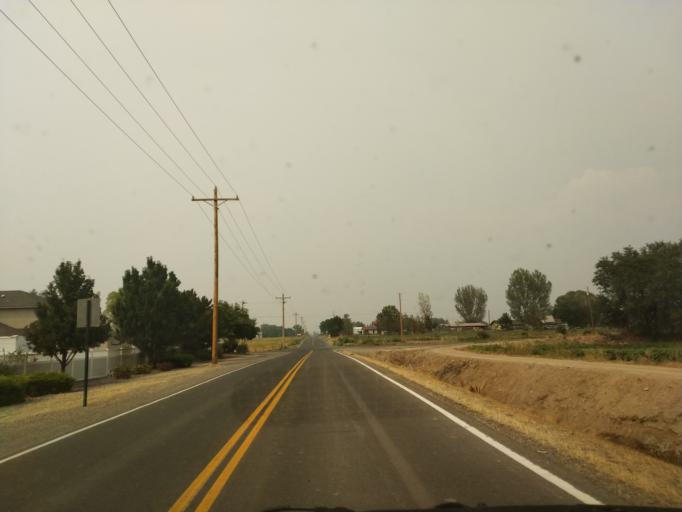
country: US
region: Colorado
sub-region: Mesa County
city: Fruitvale
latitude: 39.0329
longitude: -108.4967
